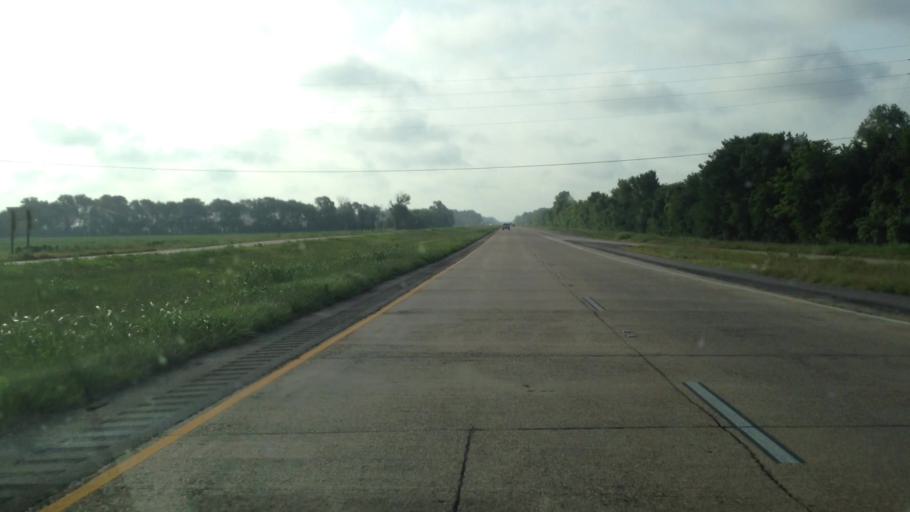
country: US
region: Louisiana
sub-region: Rapides Parish
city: Lecompte
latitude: 31.0130
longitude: -92.3725
